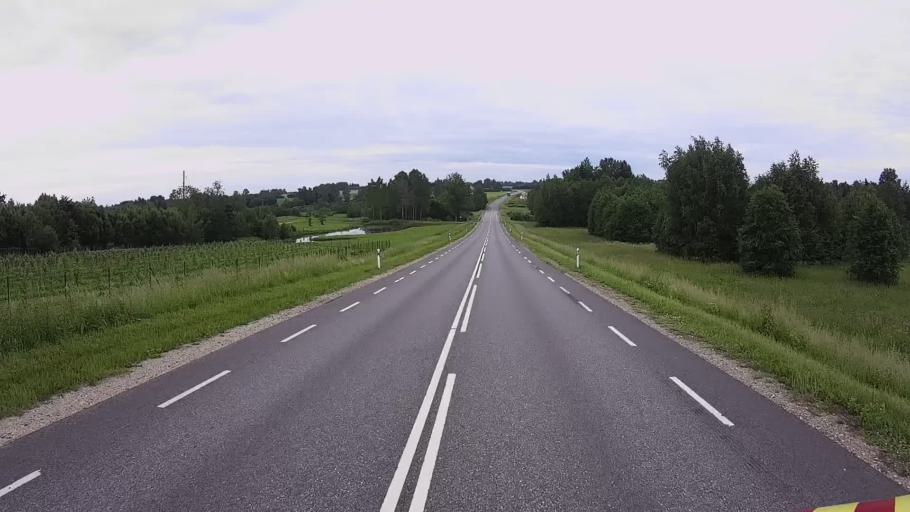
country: EE
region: Viljandimaa
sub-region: Karksi vald
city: Karksi-Nuia
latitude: 58.1500
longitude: 25.5958
